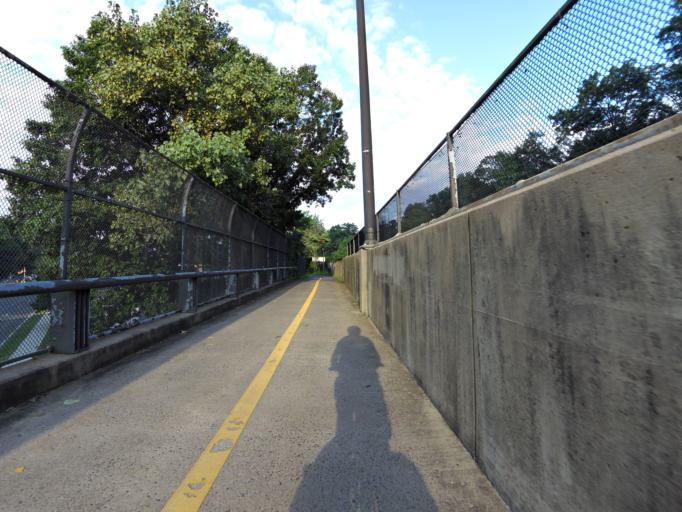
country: US
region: Virginia
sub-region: Arlington County
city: Arlington
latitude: 38.8975
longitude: -77.0946
